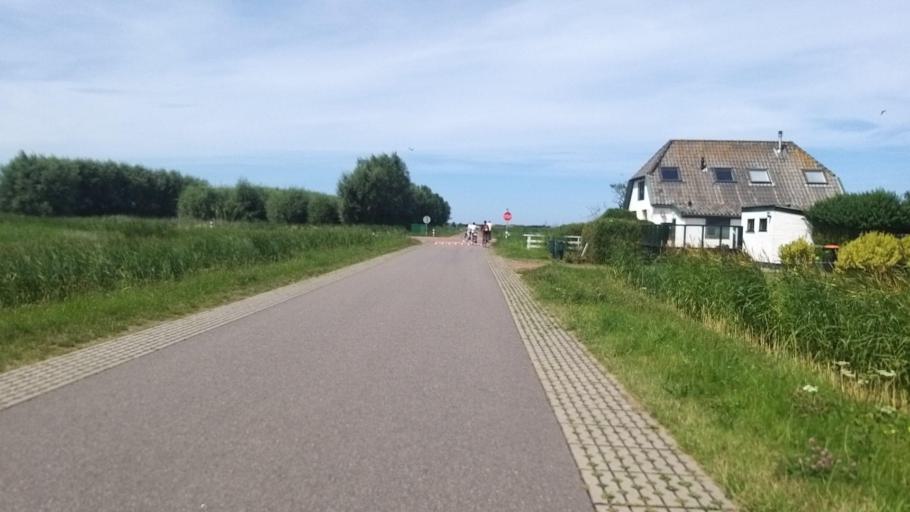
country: NL
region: North Holland
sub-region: Gemeente Texel
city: Den Burg
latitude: 53.1168
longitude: 4.8502
